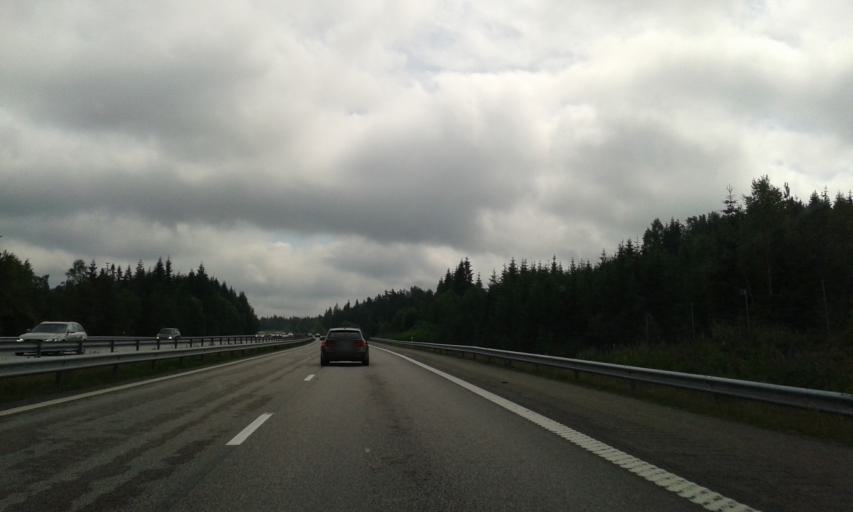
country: SE
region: Vaestra Goetaland
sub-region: Bollebygds Kommun
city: Bollebygd
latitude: 57.6701
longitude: 12.6456
